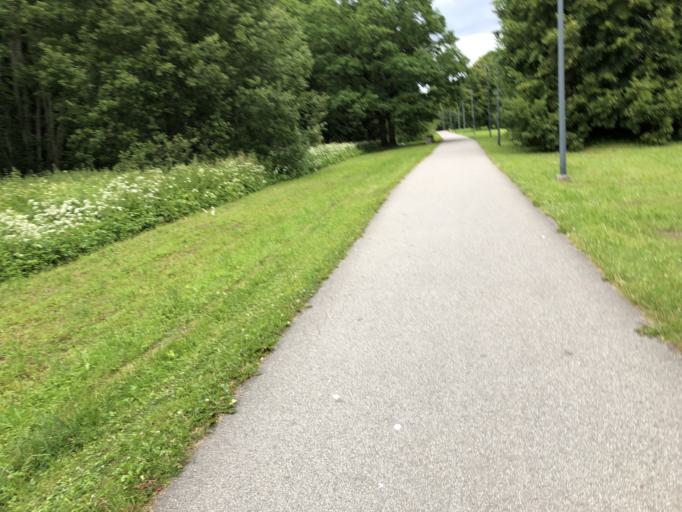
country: EE
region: Harju
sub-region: Viimsi vald
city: Viimsi
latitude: 59.4591
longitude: 24.8302
